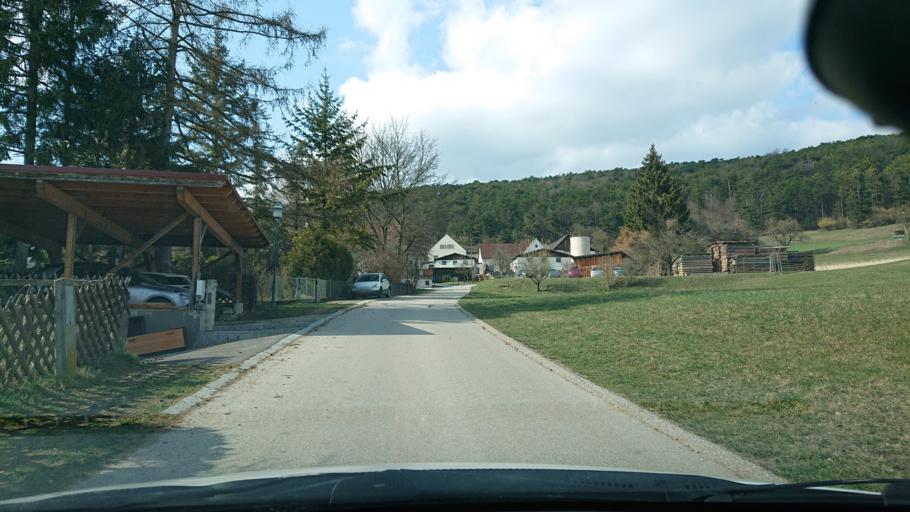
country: AT
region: Lower Austria
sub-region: Politischer Bezirk Baden
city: Pottenstein
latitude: 47.9433
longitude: 16.0675
